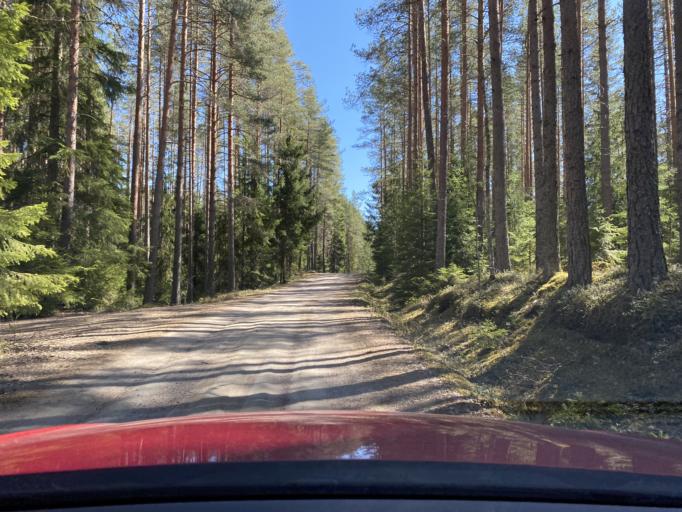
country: FI
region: Uusimaa
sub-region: Helsinki
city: Kaerkoelae
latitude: 60.6622
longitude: 23.8657
